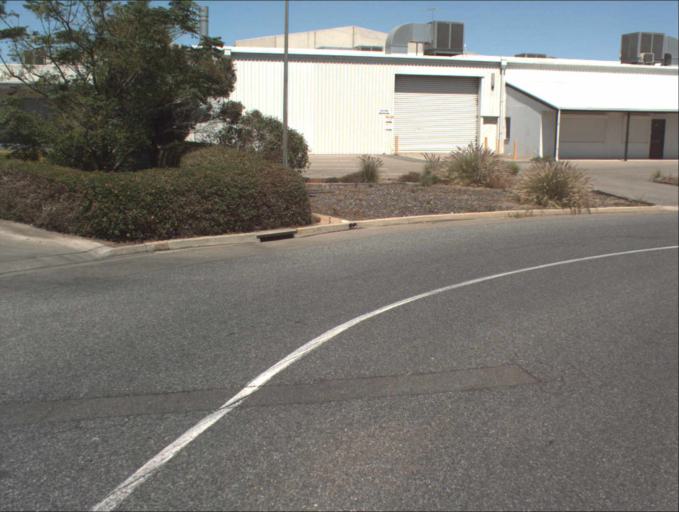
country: AU
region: South Australia
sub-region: Charles Sturt
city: West Lakes Shore
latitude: -34.8547
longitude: 138.5049
